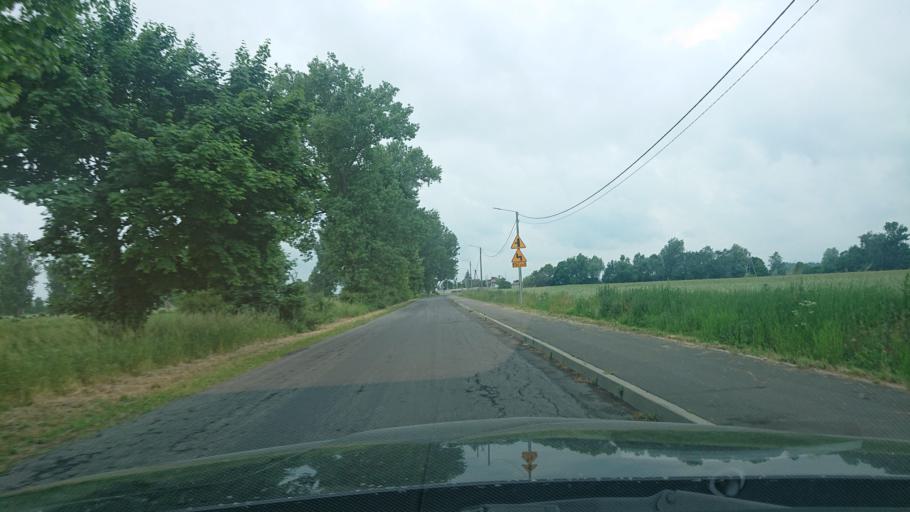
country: PL
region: Greater Poland Voivodeship
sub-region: Powiat gnieznienski
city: Gniezno
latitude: 52.4536
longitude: 17.5731
